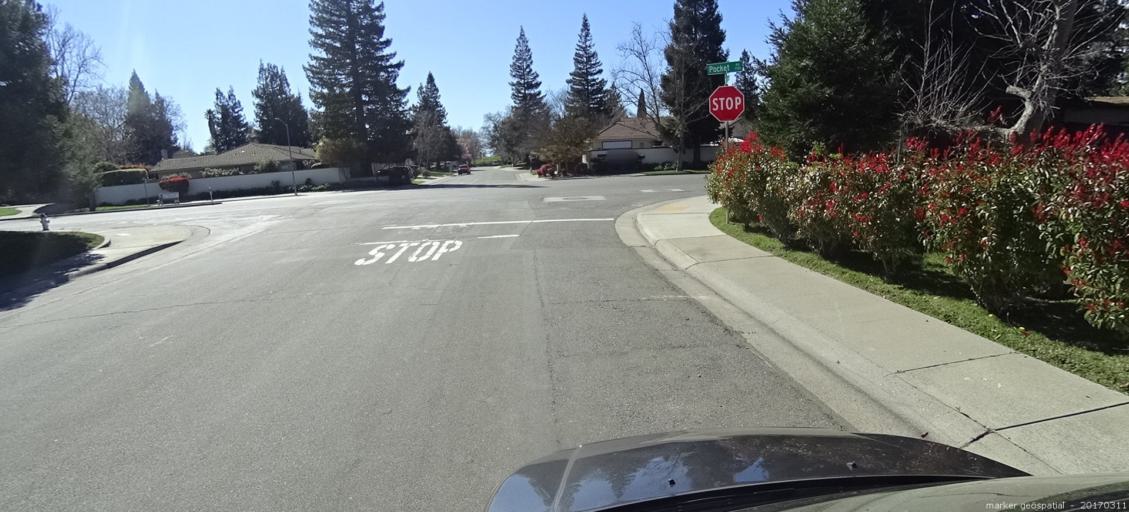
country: US
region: California
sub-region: Yolo County
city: West Sacramento
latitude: 38.4947
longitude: -121.5521
